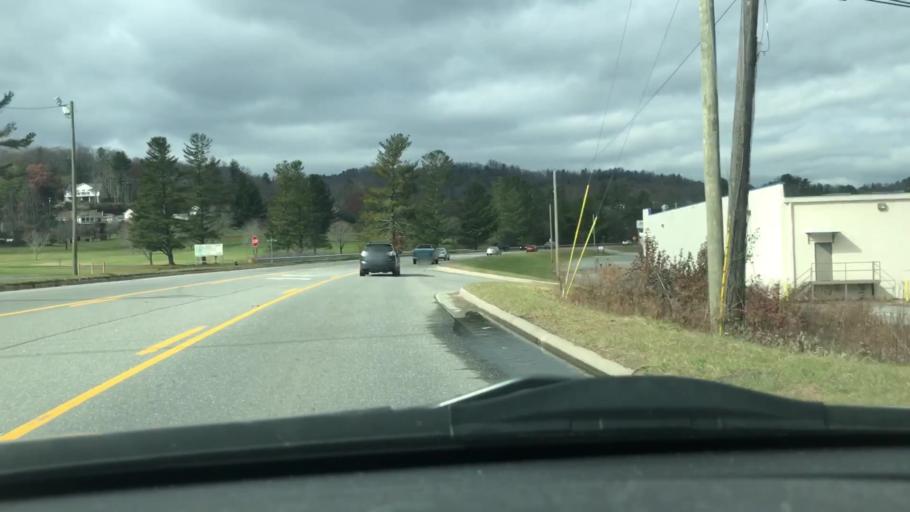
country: US
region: North Carolina
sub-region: Mitchell County
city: Spruce Pine
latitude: 35.8882
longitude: -82.0653
